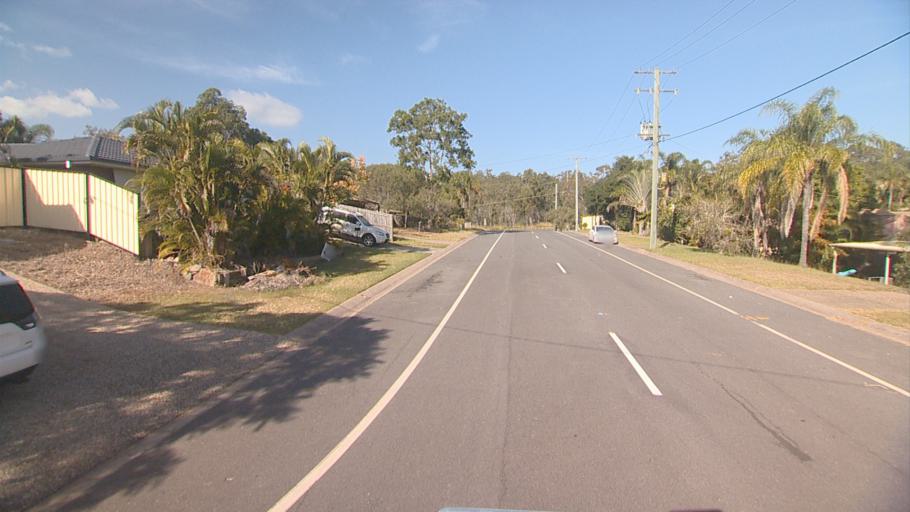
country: AU
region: Queensland
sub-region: Logan
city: Windaroo
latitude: -27.7233
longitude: 153.1811
